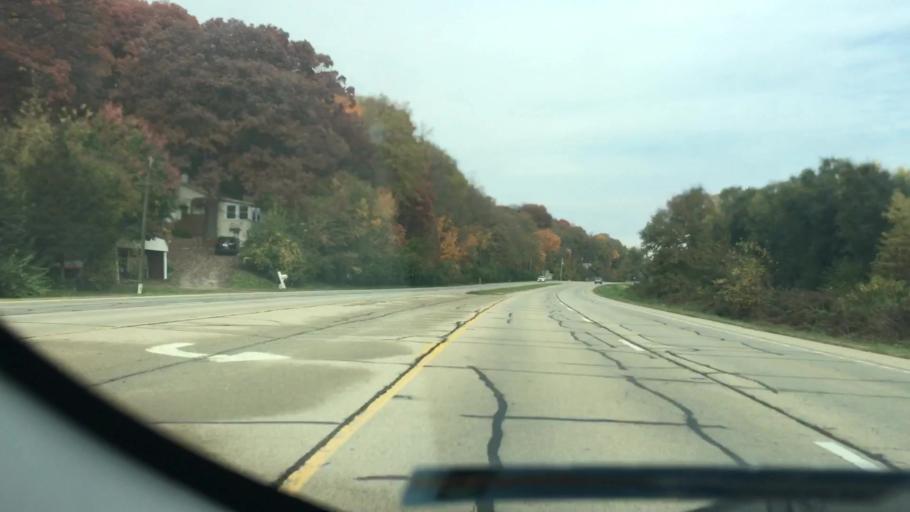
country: US
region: Illinois
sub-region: Peoria County
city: Peoria Heights
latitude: 40.7770
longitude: -89.5763
